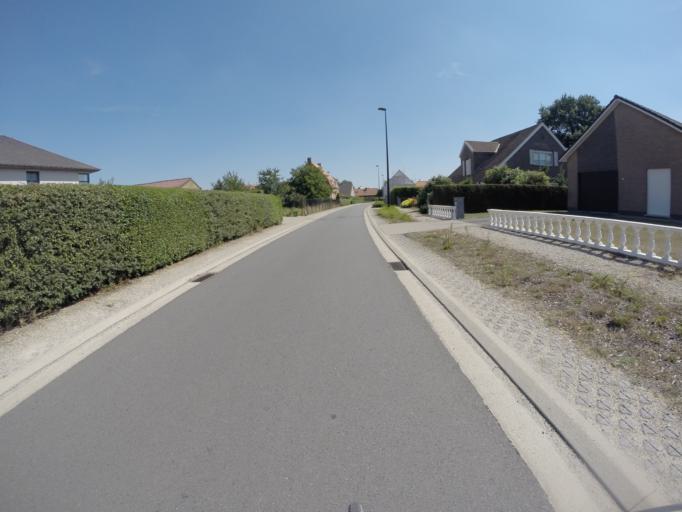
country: BE
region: Flanders
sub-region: Provincie Oost-Vlaanderen
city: Knesselare
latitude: 51.1427
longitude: 3.4192
